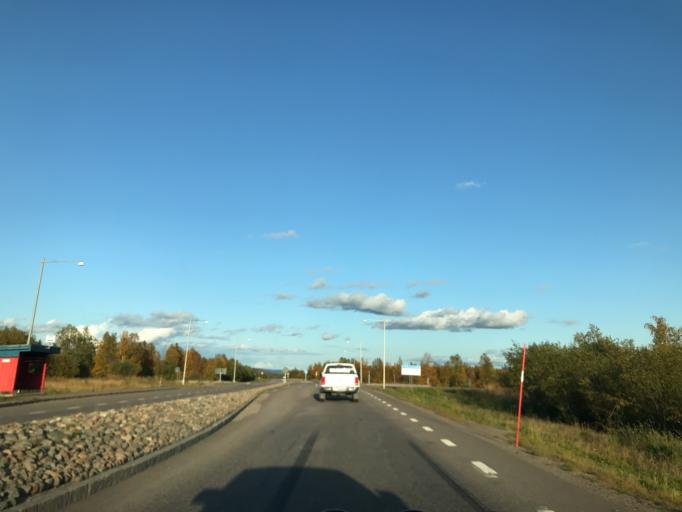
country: SE
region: Norrbotten
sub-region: Kiruna Kommun
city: Kiruna
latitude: 67.8456
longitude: 20.3464
